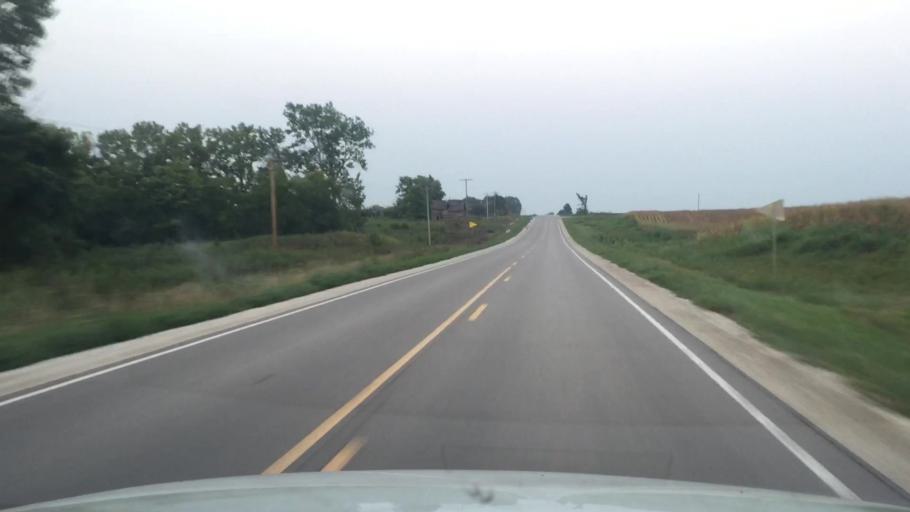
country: US
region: Iowa
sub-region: Warren County
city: Indianola
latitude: 41.1826
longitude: -93.4844
